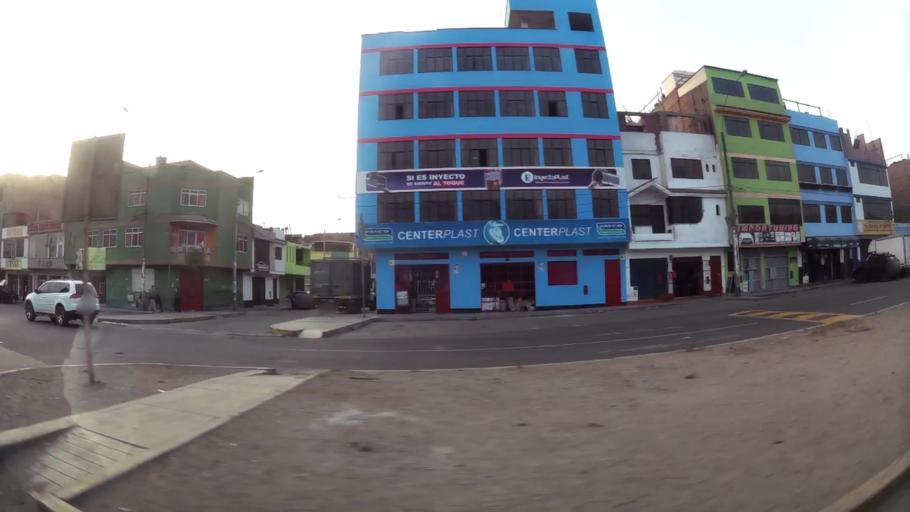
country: PE
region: Lima
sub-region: Lima
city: Independencia
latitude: -12.0124
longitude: -77.0782
